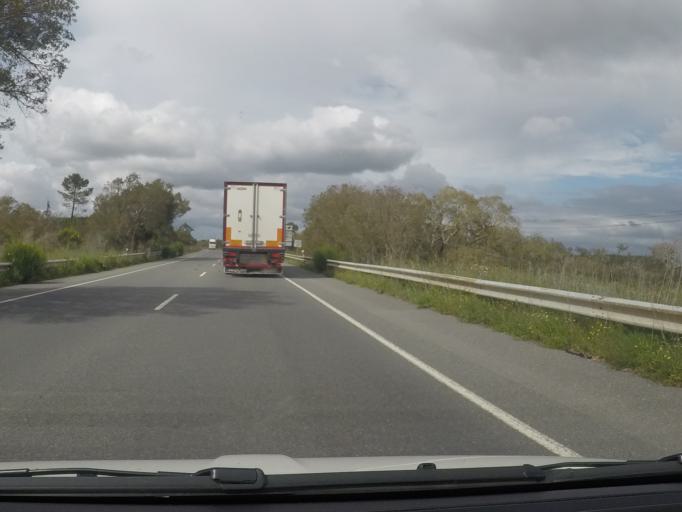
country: PT
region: Setubal
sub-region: Grandola
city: Grandola
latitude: 38.1459
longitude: -8.6503
